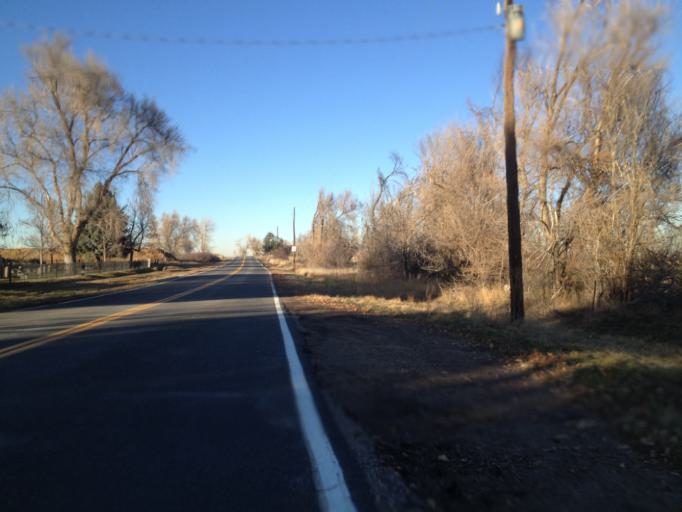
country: US
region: Colorado
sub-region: Boulder County
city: Louisville
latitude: 39.9729
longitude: -105.1093
